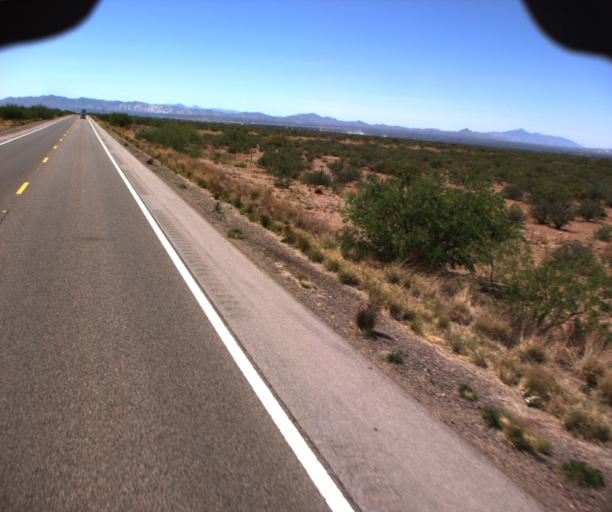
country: US
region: Arizona
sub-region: Cochise County
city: Douglas
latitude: 31.4076
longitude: -109.4997
